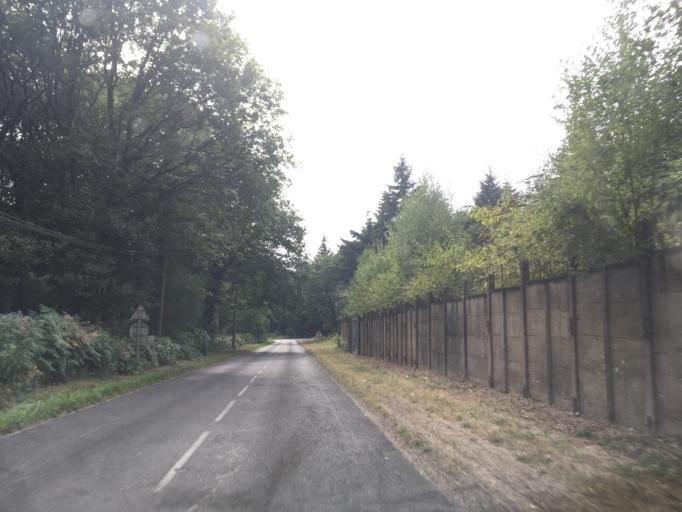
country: FR
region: Haute-Normandie
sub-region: Departement de l'Eure
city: Vernon
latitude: 49.1067
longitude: 1.5114
